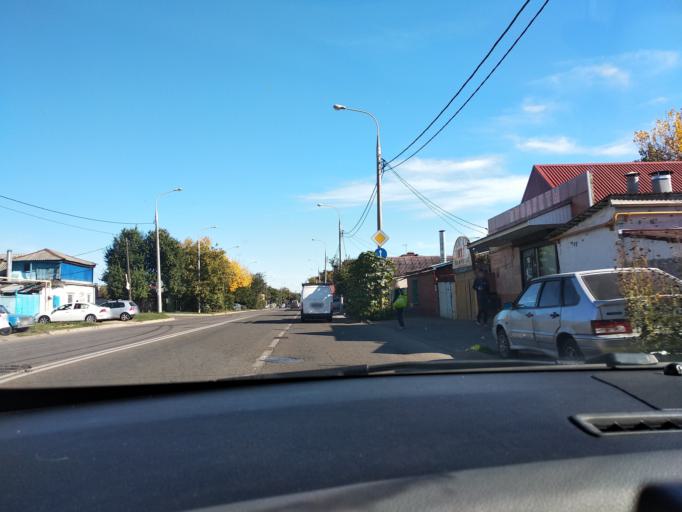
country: RU
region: Krasnodarskiy
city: Krasnodar
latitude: 45.0161
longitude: 38.9948
